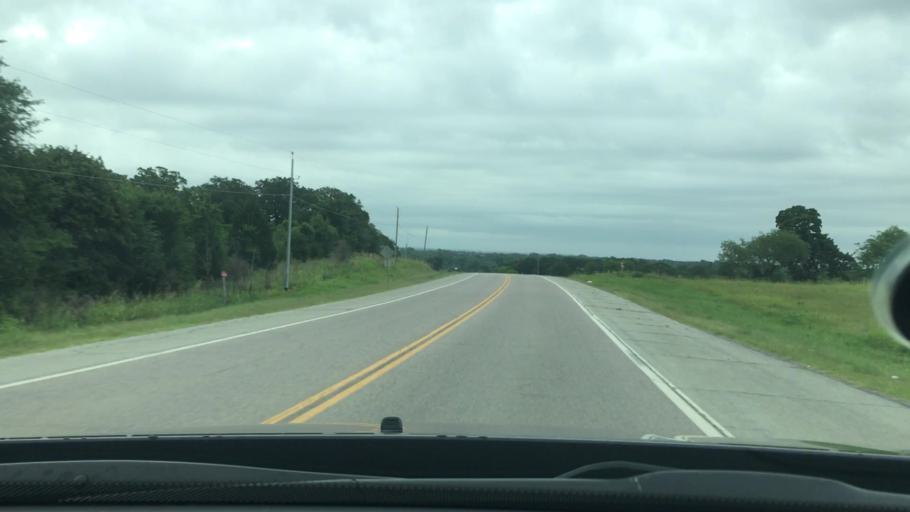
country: US
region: Oklahoma
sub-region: Coal County
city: Coalgate
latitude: 34.5542
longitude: -96.2388
